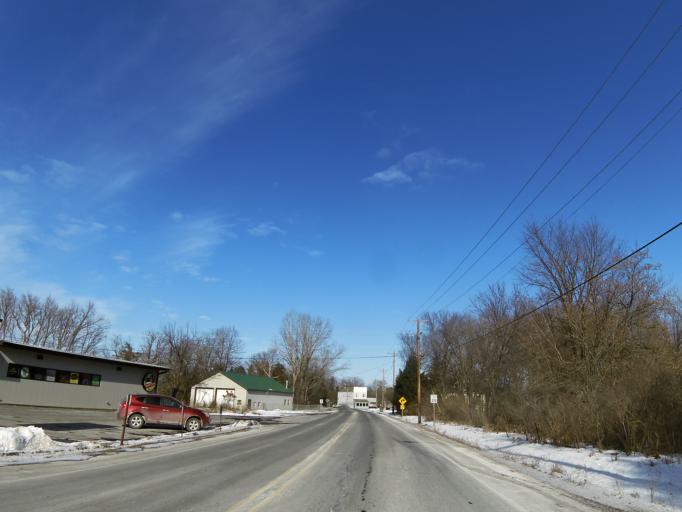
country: US
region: Wisconsin
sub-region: Saint Croix County
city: North Hudson
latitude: 45.0199
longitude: -92.6686
